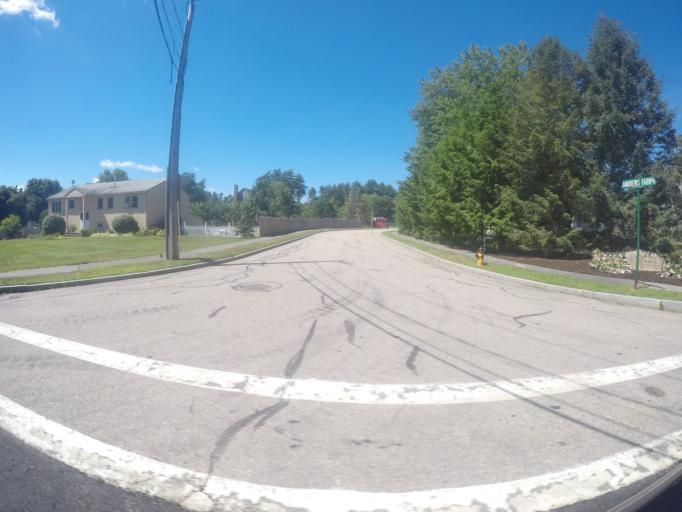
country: US
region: Massachusetts
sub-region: Bristol County
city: Easton
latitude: 42.0579
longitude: -71.1274
